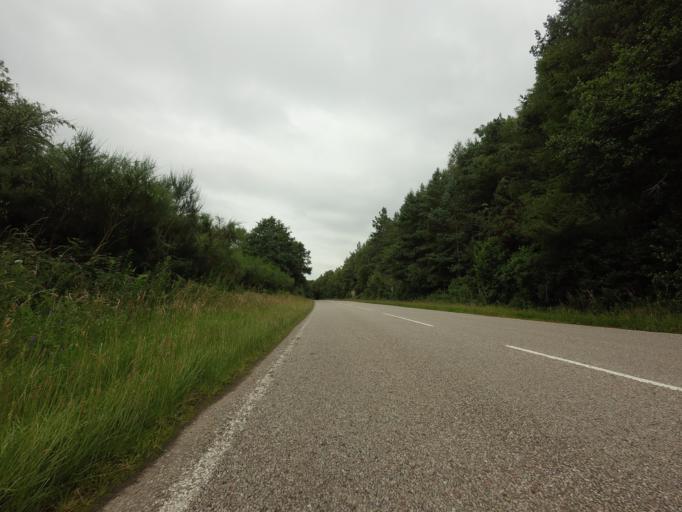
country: GB
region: Scotland
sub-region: Highland
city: Alness
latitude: 57.9076
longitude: -4.3622
